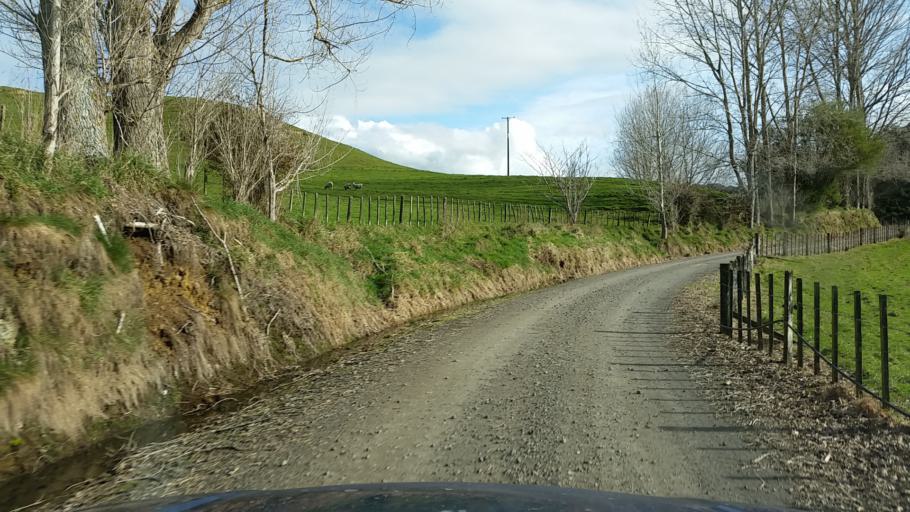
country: NZ
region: Taranaki
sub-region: South Taranaki District
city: Eltham
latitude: -39.2602
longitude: 174.5861
